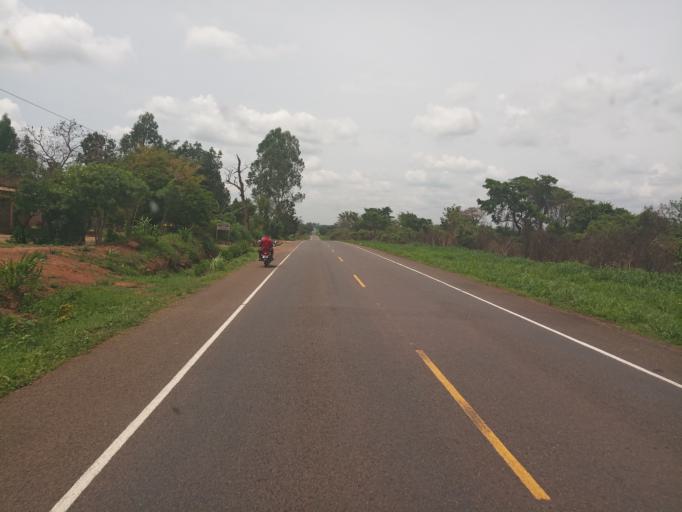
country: UG
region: Northern Region
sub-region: Oyam District
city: Oyam
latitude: 2.1761
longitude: 32.2240
